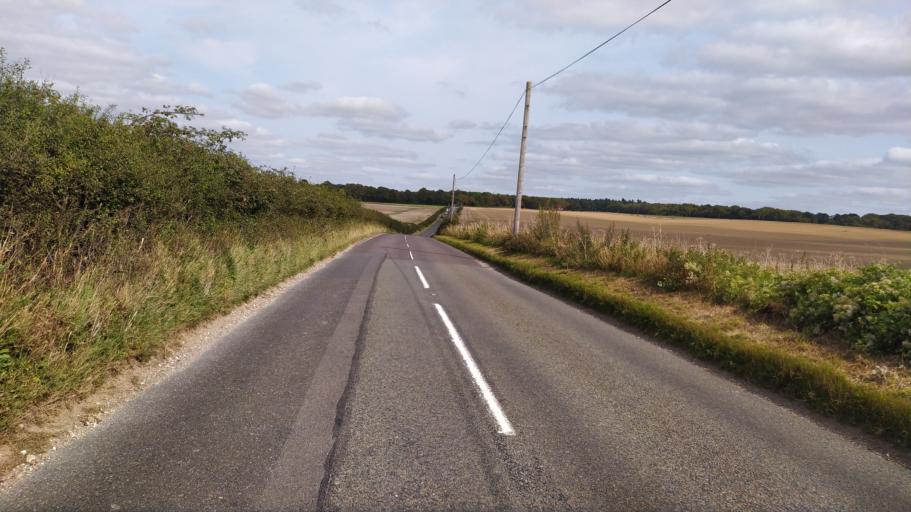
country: GB
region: England
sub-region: Dorset
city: Three Legged Cross
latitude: 50.8916
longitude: -1.9637
